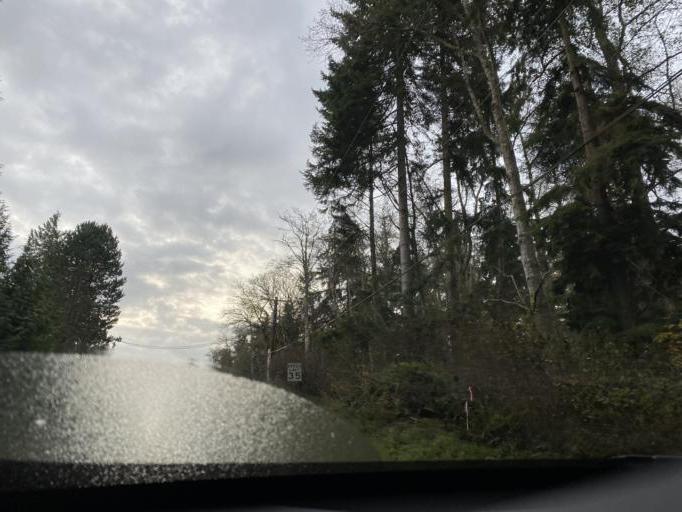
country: US
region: Washington
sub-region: Island County
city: Camano
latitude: 48.0933
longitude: -122.4928
